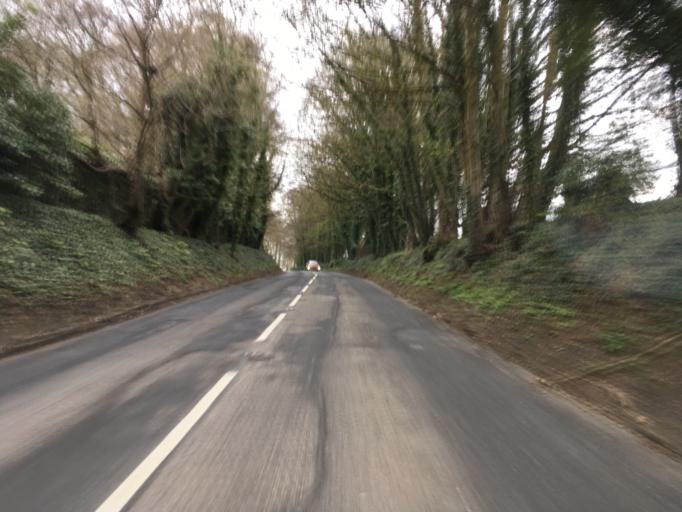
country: GB
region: England
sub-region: Gloucestershire
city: Northleach
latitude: 51.7602
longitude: -1.8286
